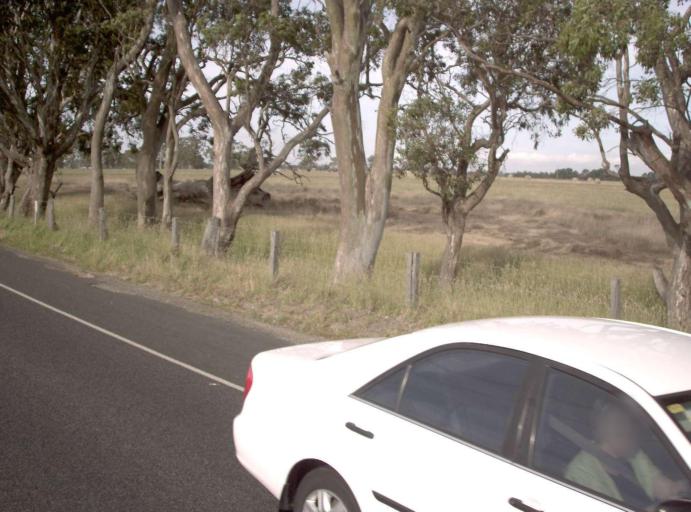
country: AU
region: Victoria
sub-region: Latrobe
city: Traralgon
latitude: -38.1459
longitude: 146.5555
